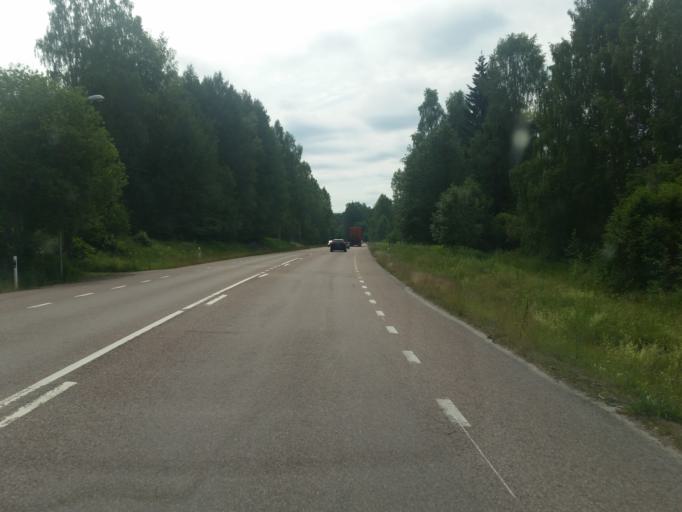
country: SE
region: Dalarna
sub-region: Gagnefs Kommun
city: Djuras
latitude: 60.5447
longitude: 15.2785
